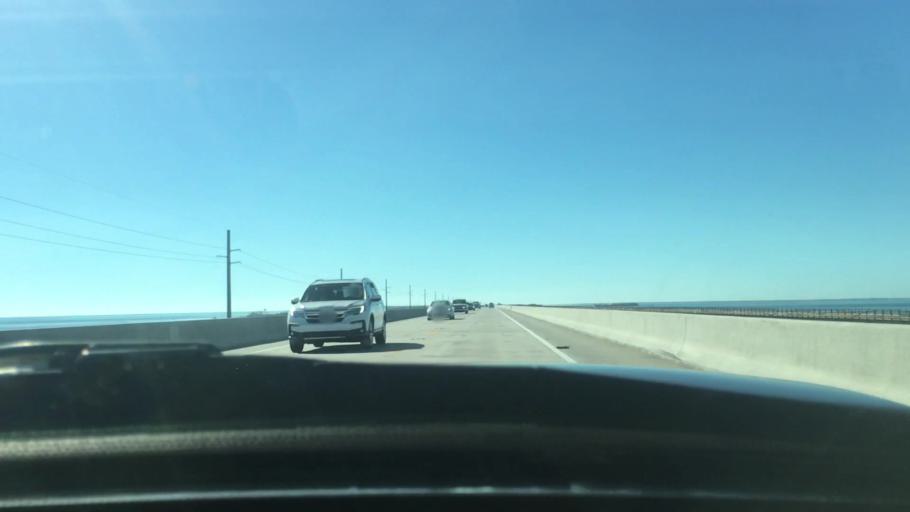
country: US
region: Florida
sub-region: Monroe County
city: Marathon
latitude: 24.6889
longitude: -81.2059
